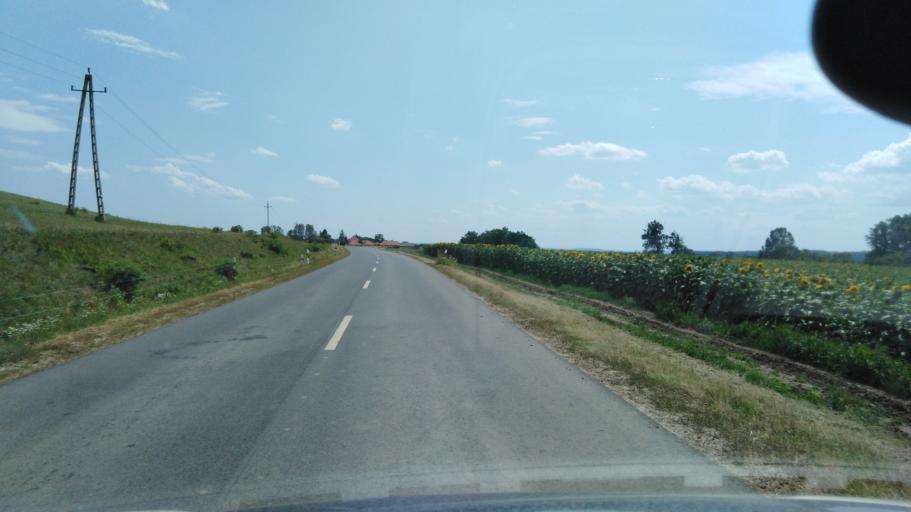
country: HU
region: Nograd
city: Szecseny
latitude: 48.1577
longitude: 19.5343
